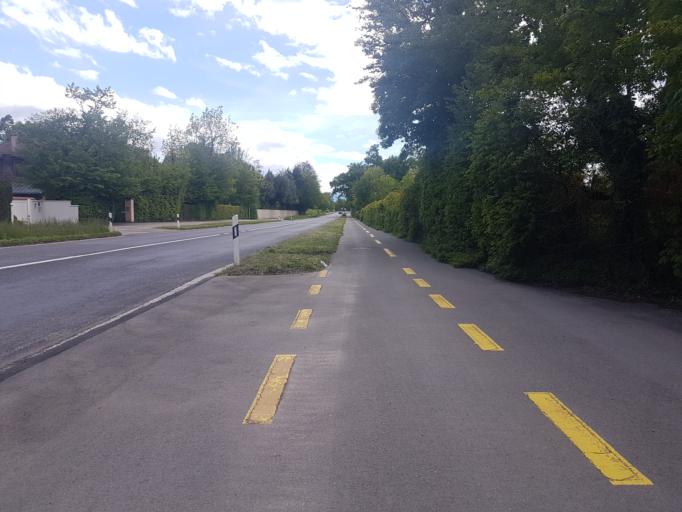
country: CH
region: Vaud
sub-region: Nyon District
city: Founex
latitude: 46.3472
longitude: 6.2064
